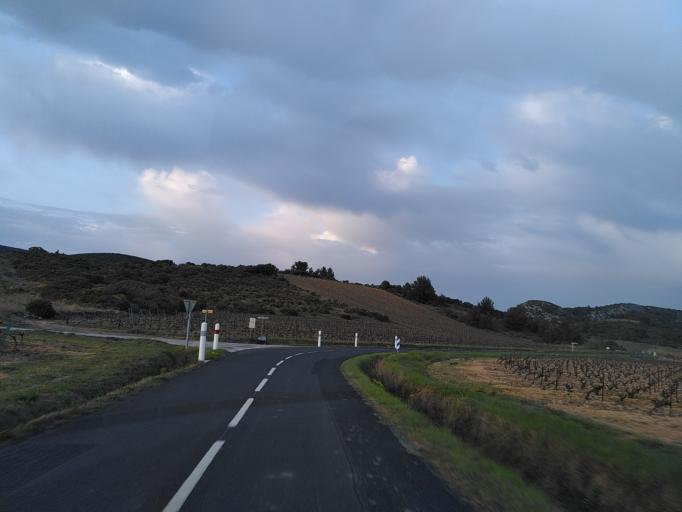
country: FR
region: Languedoc-Roussillon
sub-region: Departement des Pyrenees-Orientales
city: Estagel
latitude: 42.8183
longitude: 2.7055
